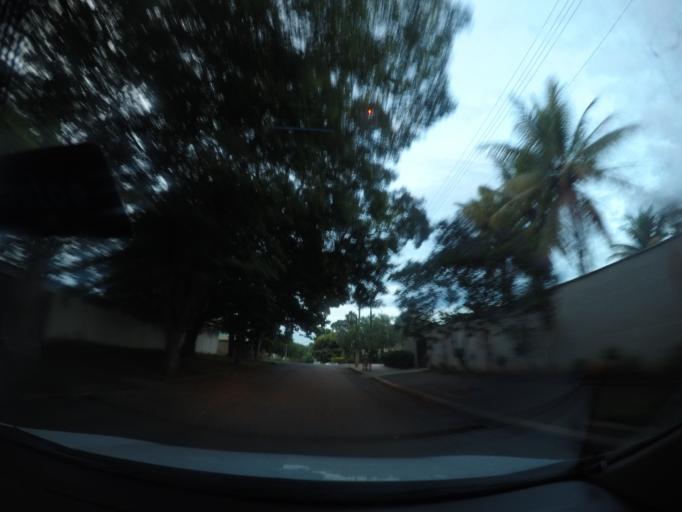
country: BR
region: Goias
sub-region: Goiania
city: Goiania
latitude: -16.6491
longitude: -49.2263
